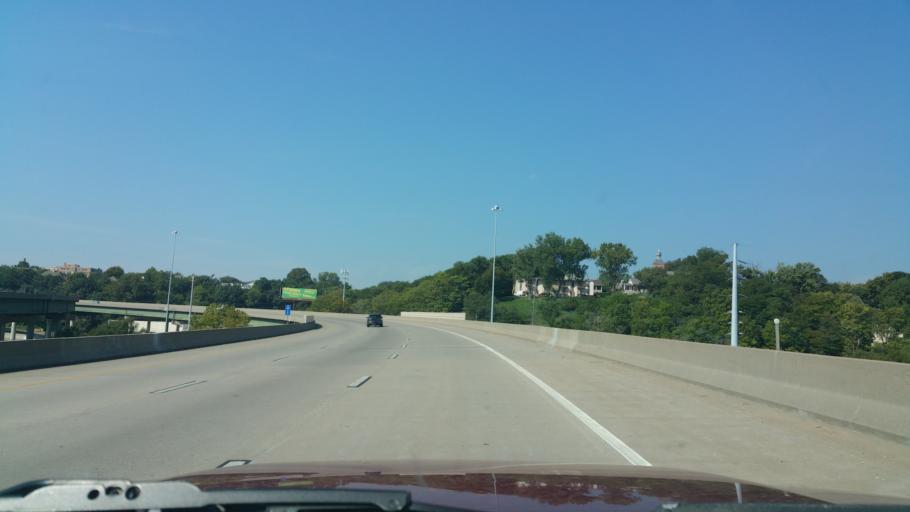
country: US
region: Kansas
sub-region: Wyandotte County
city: Kansas City
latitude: 39.1001
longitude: -94.6199
